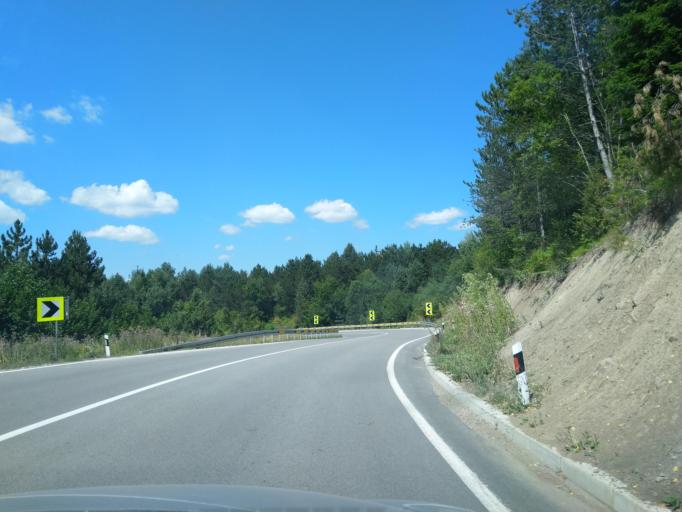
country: RS
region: Central Serbia
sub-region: Zlatiborski Okrug
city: Sjenica
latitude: 43.3130
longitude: 19.8962
